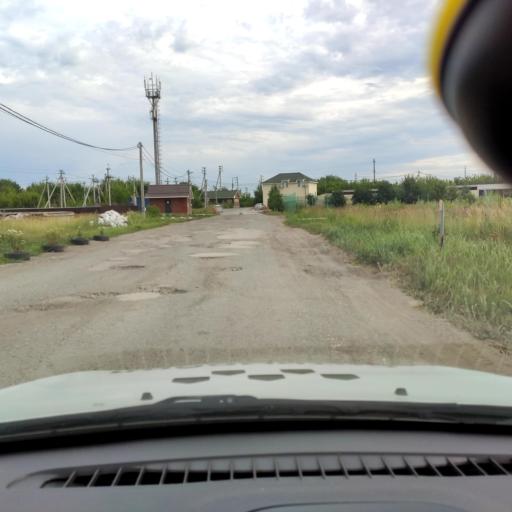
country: RU
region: Samara
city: Podstepki
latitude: 53.5753
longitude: 49.0810
